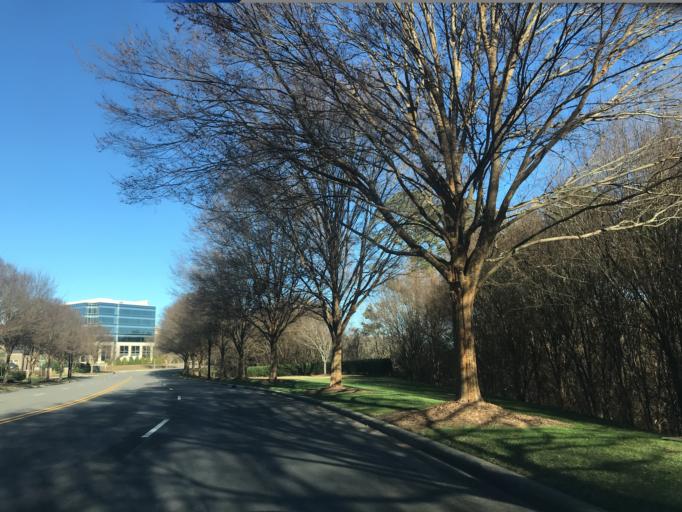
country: US
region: North Carolina
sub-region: Wake County
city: West Raleigh
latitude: 35.8324
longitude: -78.6912
